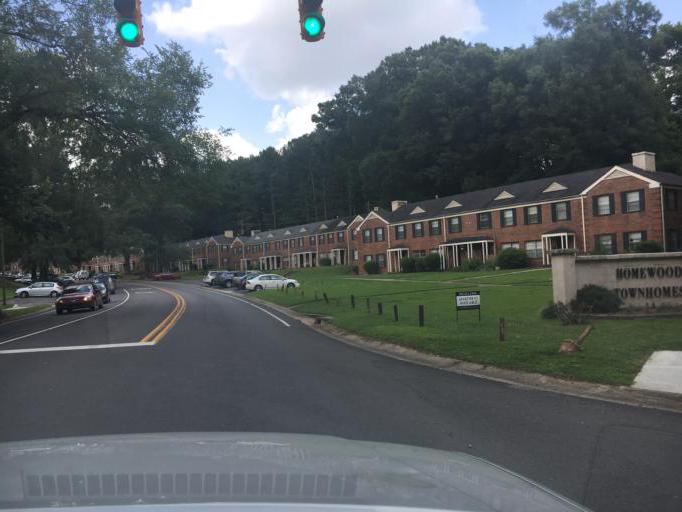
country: US
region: Alabama
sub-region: Jefferson County
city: Homewood
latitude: 33.4828
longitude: -86.8015
